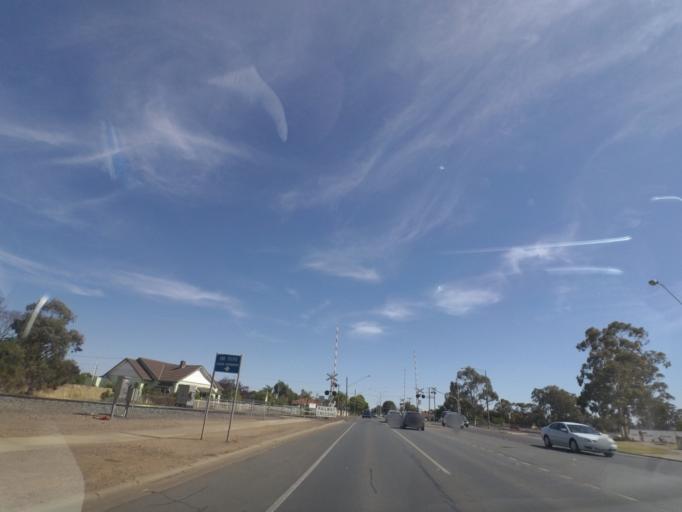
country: AU
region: Victoria
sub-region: Greater Shepparton
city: Shepparton
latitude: -36.3912
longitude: 145.3973
